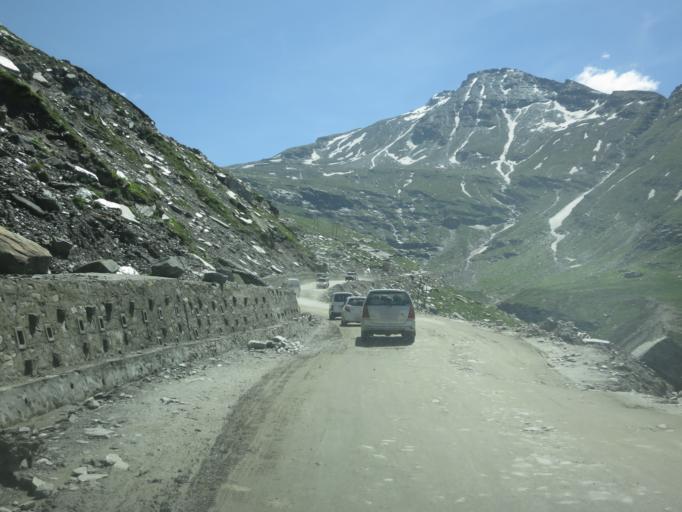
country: IN
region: Himachal Pradesh
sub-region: Kulu
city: Manali
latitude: 32.3558
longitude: 77.2262
